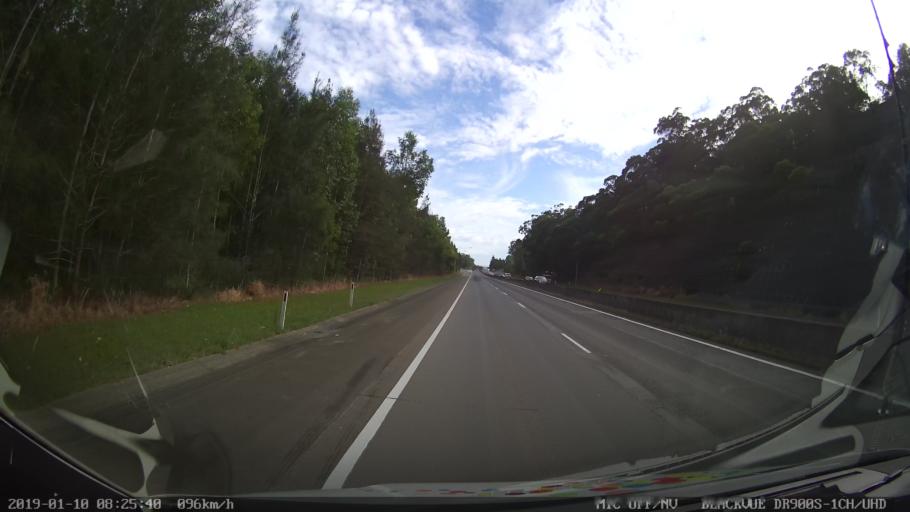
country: AU
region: New South Wales
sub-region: Coffs Harbour
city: Bonville
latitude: -30.4308
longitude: 153.0185
